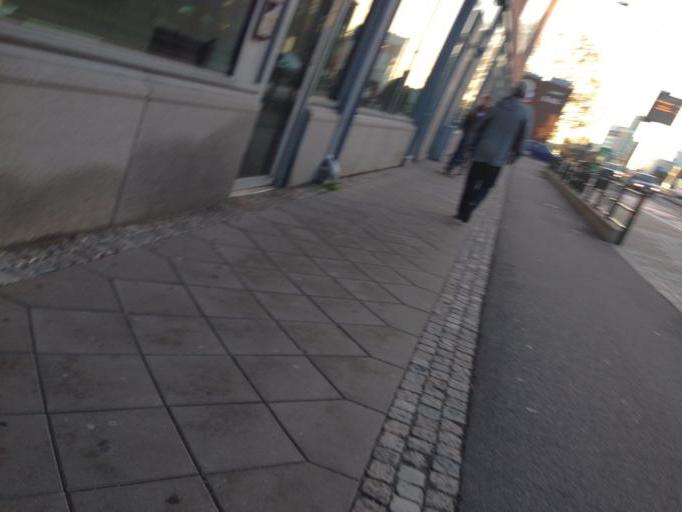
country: SE
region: Skane
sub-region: Malmo
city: Malmoe
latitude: 55.6127
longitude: 12.9911
